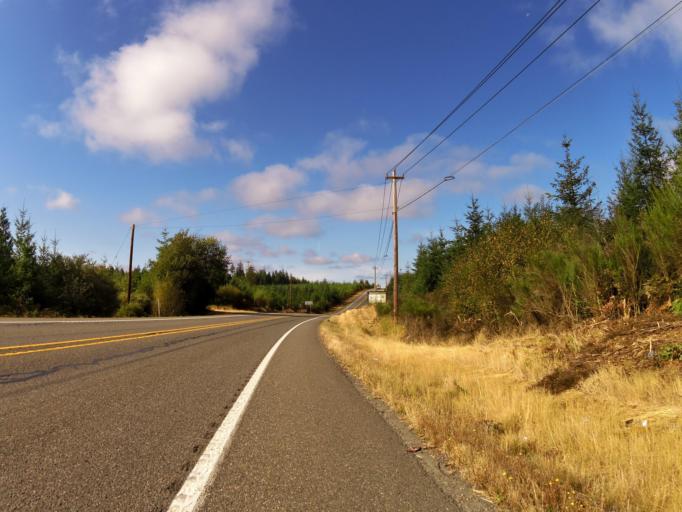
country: US
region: Washington
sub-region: Mason County
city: Allyn
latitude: 47.3337
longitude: -122.8731
